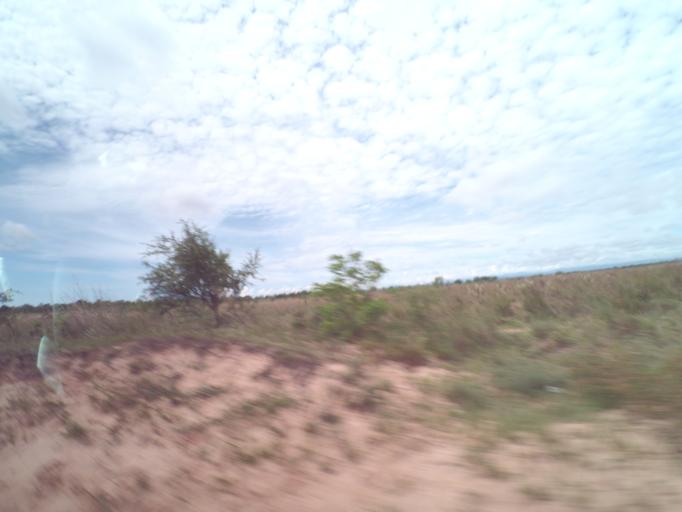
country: BO
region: Santa Cruz
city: Santa Cruz de la Sierra
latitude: -17.9120
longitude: -63.1646
